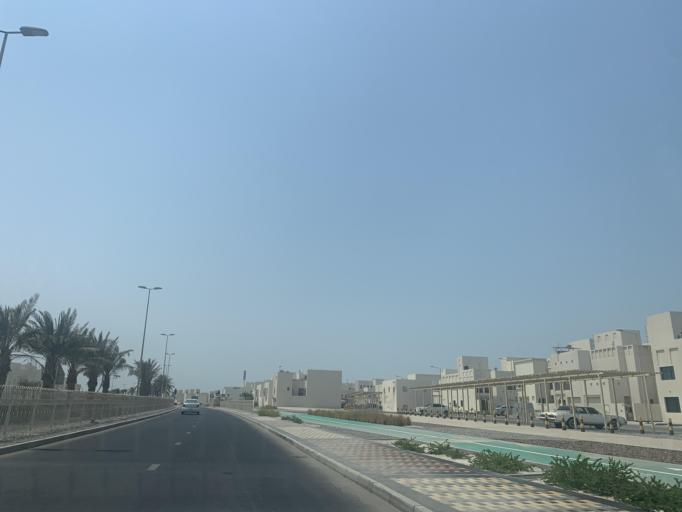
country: BH
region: Muharraq
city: Al Hadd
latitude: 26.2328
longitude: 50.6703
